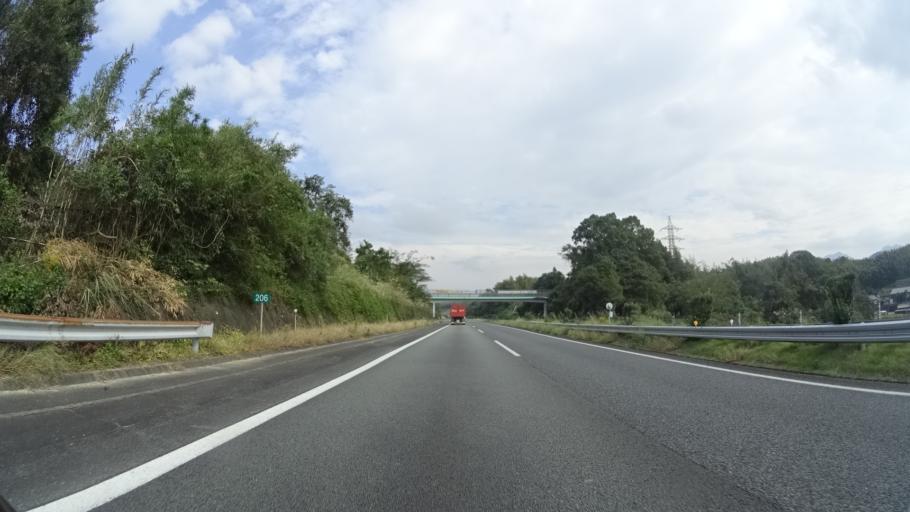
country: JP
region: Kumamoto
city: Matsubase
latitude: 32.5626
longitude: 130.6995
